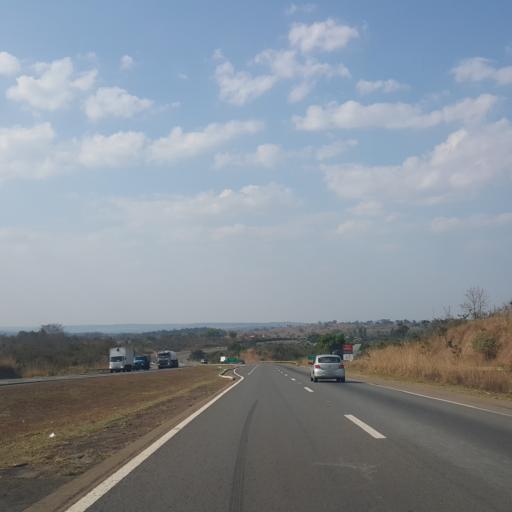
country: BR
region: Goias
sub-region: Abadiania
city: Abadiania
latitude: -16.1807
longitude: -48.6526
